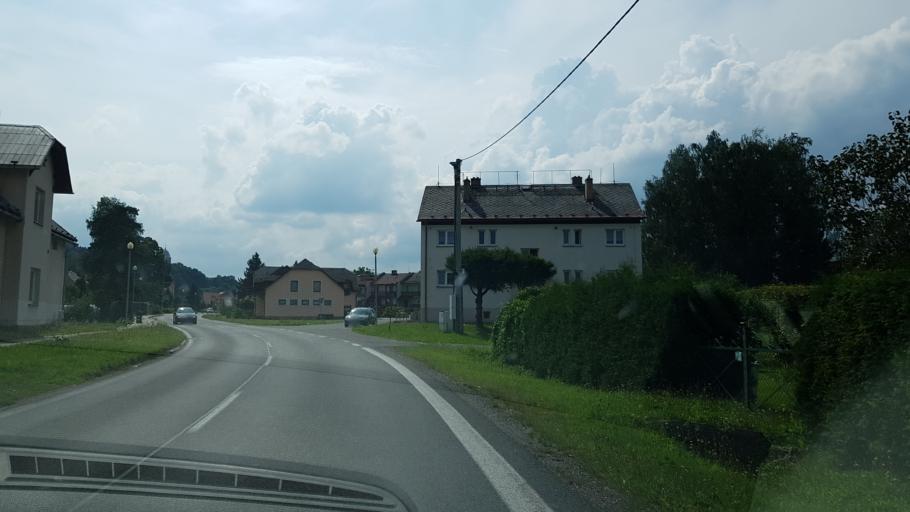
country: CZ
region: Olomoucky
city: Ceska Ves
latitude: 50.2556
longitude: 17.2247
